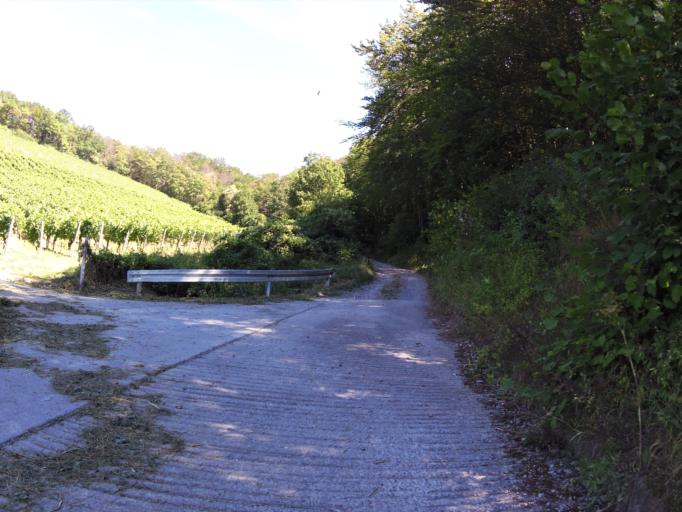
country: DE
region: Bavaria
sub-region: Regierungsbezirk Unterfranken
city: Margetshochheim
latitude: 49.8601
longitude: 9.8674
